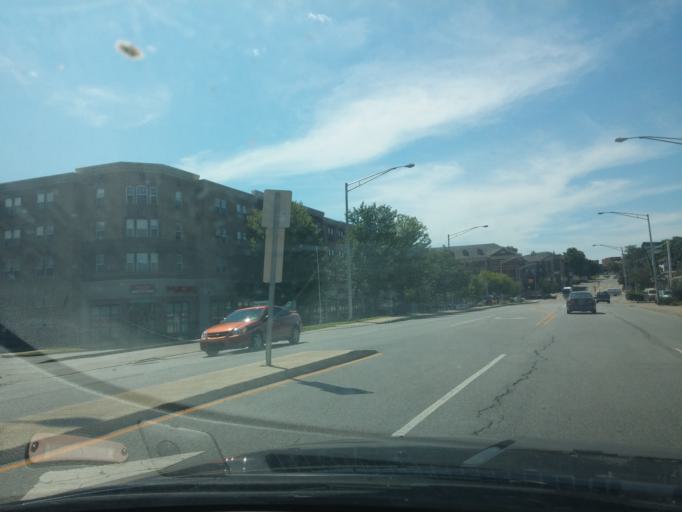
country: US
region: Indiana
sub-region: Tippecanoe County
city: West Lafayette
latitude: 40.4212
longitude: -86.9021
